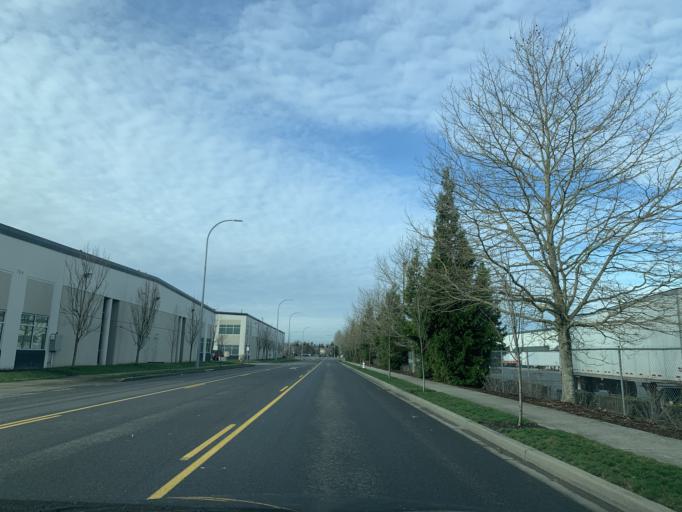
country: US
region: Washington
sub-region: Pierce County
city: Milton
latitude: 47.2336
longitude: -122.3326
